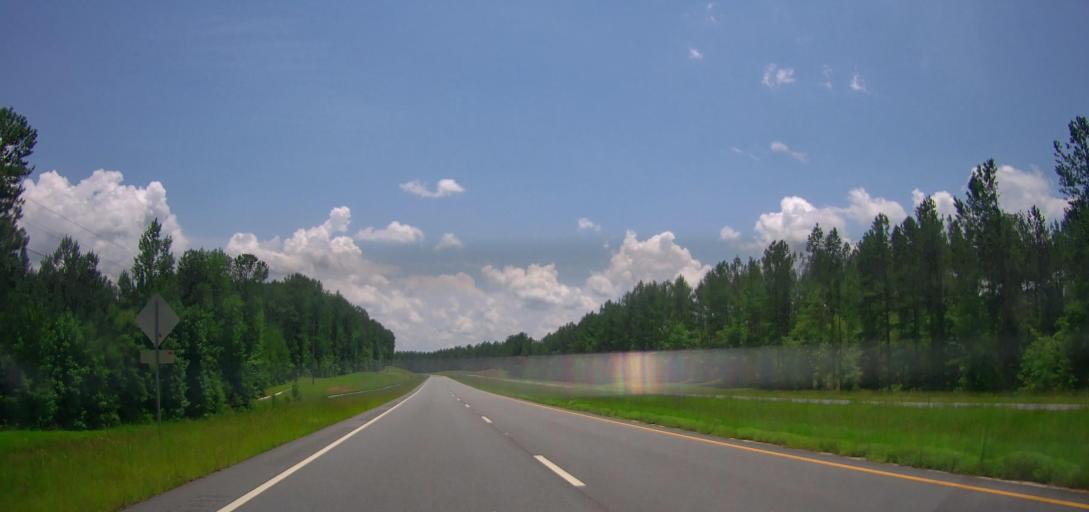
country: US
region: Georgia
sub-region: Upson County
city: Thomaston
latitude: 32.8023
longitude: -84.2751
